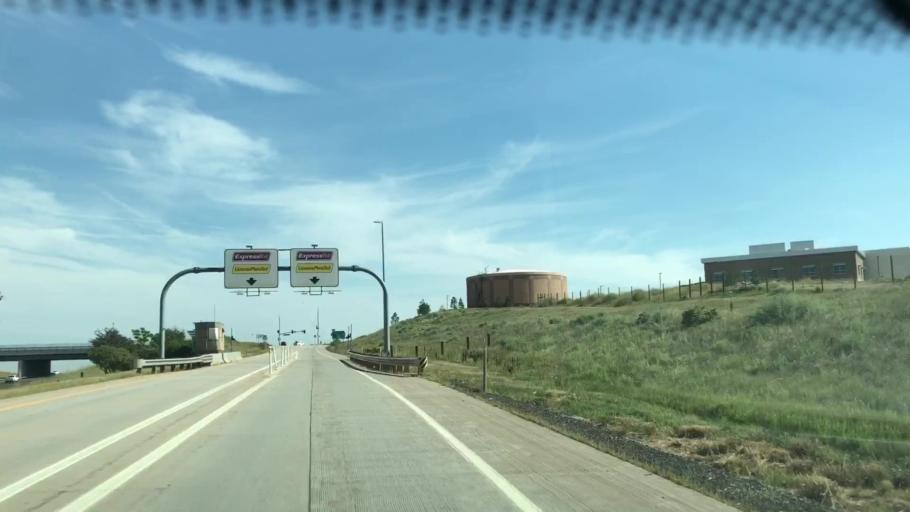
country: US
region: Colorado
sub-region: Douglas County
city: Parker
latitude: 39.5983
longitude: -104.7149
